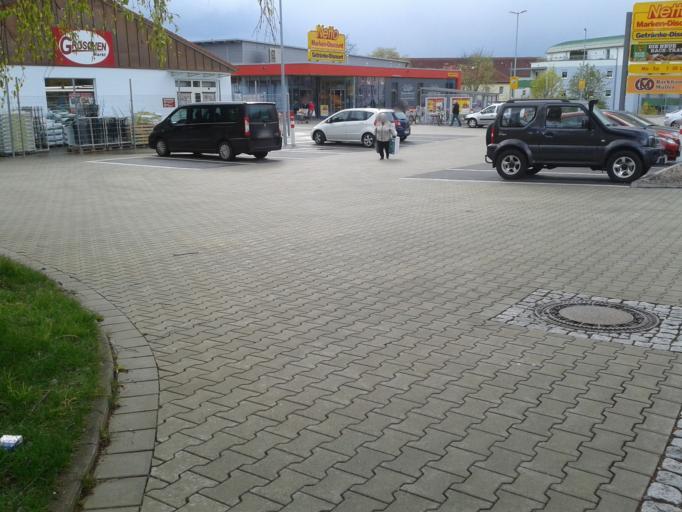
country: DE
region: Thuringia
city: Sonneberg
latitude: 50.3538
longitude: 11.1684
